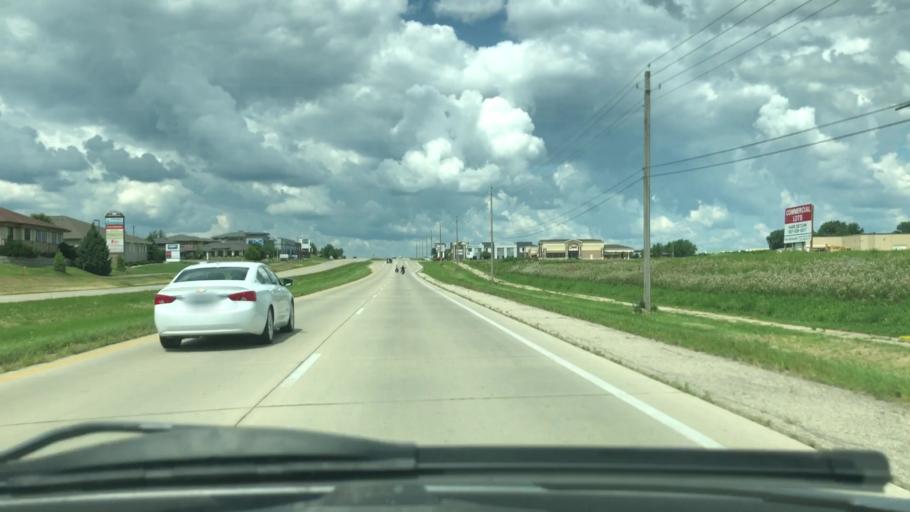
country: US
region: Minnesota
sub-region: Olmsted County
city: Rochester
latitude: 44.0479
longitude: -92.5212
